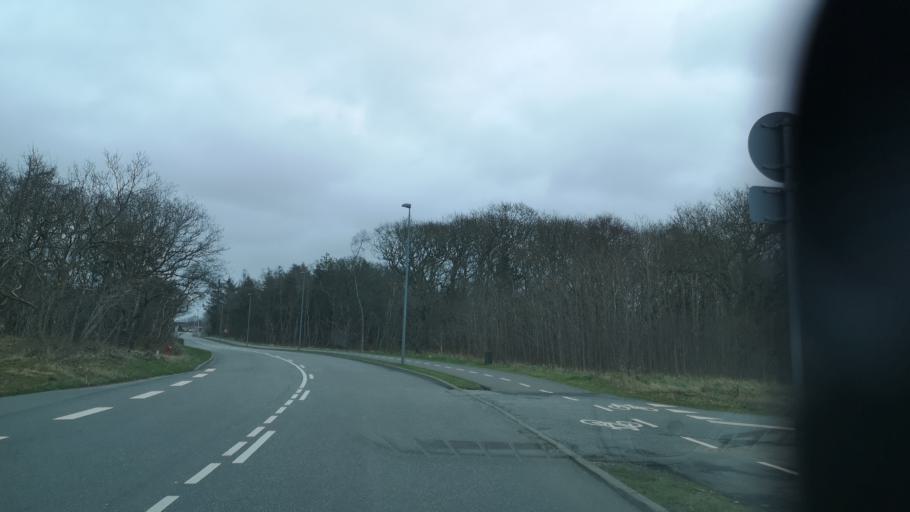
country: DK
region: Central Jutland
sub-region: Ringkobing-Skjern Kommune
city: Skjern
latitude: 55.9341
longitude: 8.5003
